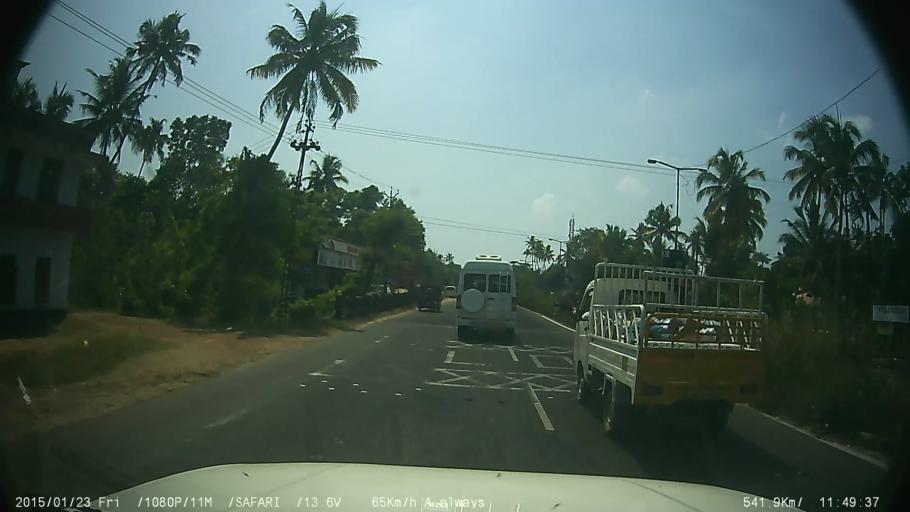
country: IN
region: Kerala
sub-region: Alappuzha
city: Vayalar
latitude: 9.7074
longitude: 76.3169
